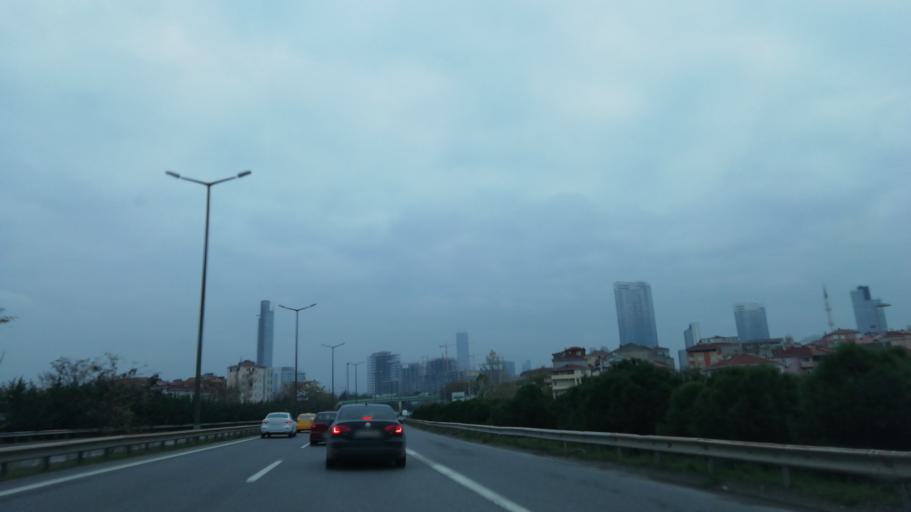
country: TR
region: Istanbul
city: Umraniye
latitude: 41.0086
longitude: 29.0939
